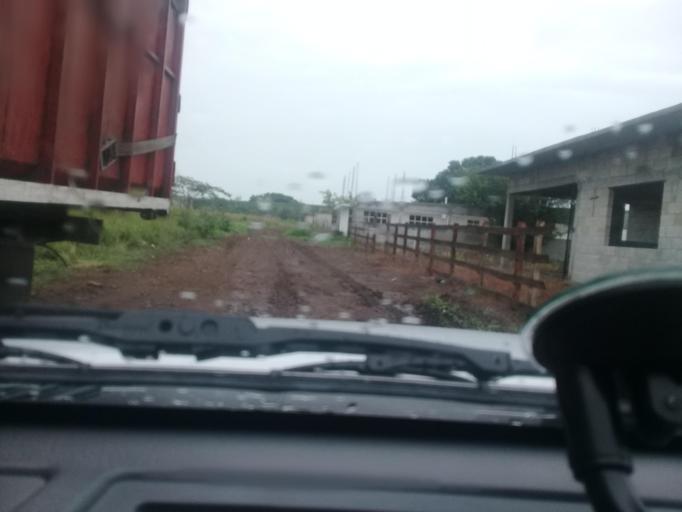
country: MX
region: Veracruz
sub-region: Puente Nacional
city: Cabezas
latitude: 19.3656
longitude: -96.3880
